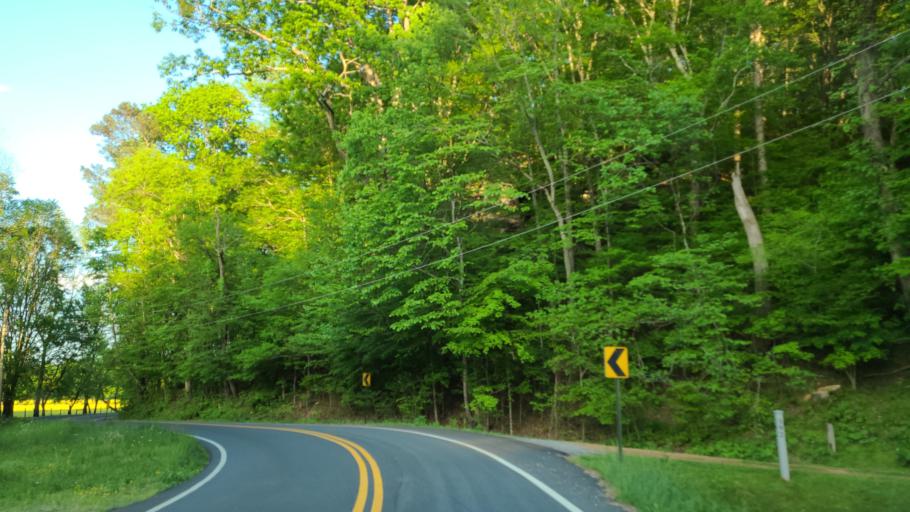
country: US
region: Georgia
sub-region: Bartow County
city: Emerson
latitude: 34.1017
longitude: -84.7774
